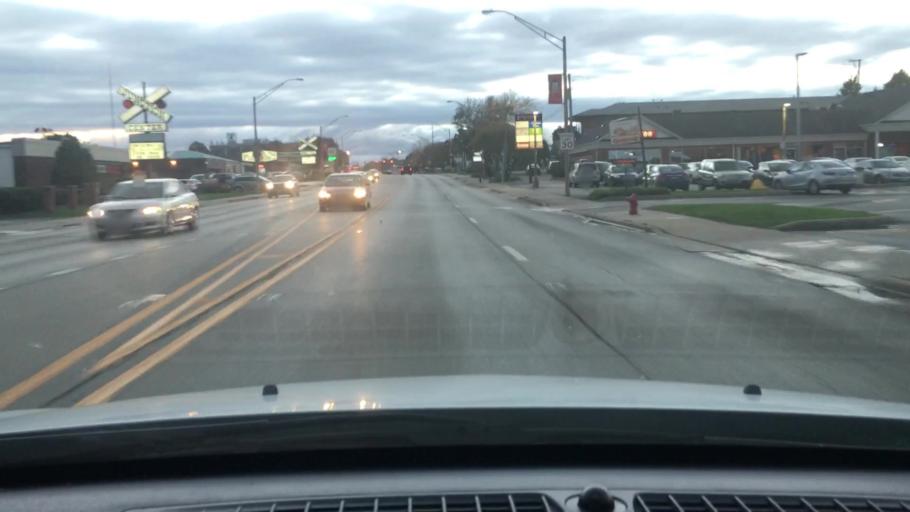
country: US
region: Illinois
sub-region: DeKalb County
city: DeKalb
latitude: 41.9311
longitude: -88.7680
